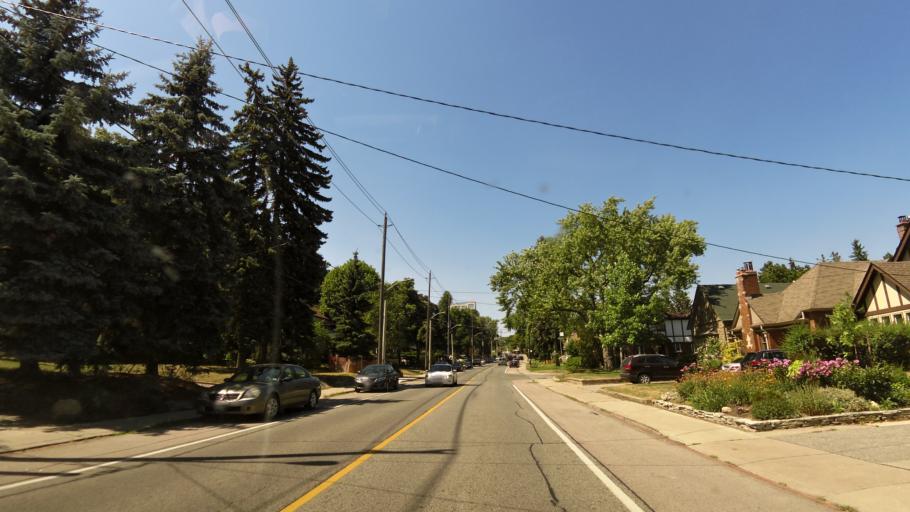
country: CA
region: Ontario
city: Etobicoke
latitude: 43.6456
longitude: -79.4830
